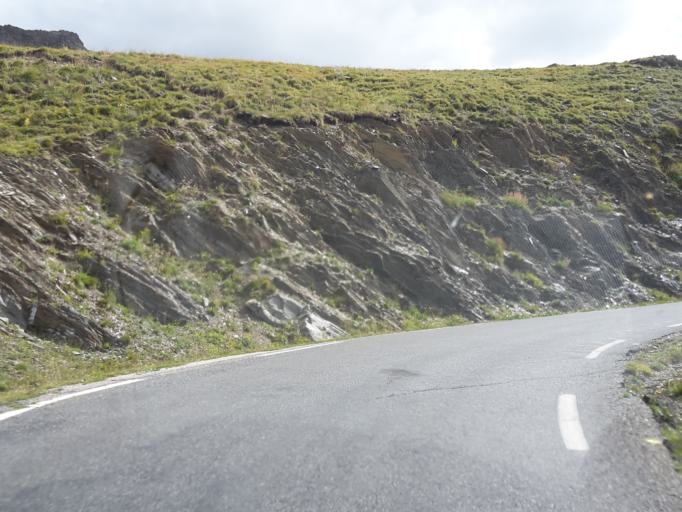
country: FR
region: Rhone-Alpes
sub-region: Departement de la Savoie
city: Valloire
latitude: 45.0524
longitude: 6.3898
